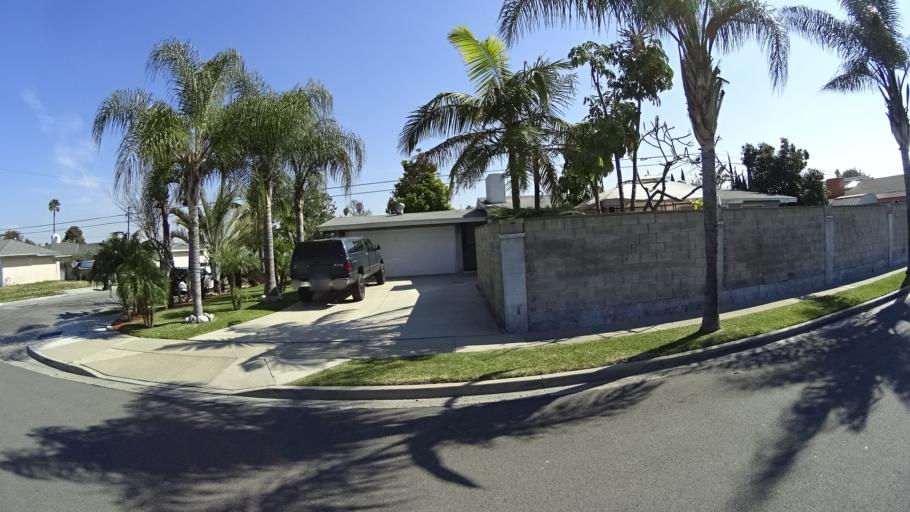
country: US
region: California
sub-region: Orange County
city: Buena Park
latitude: 33.8516
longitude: -117.9645
